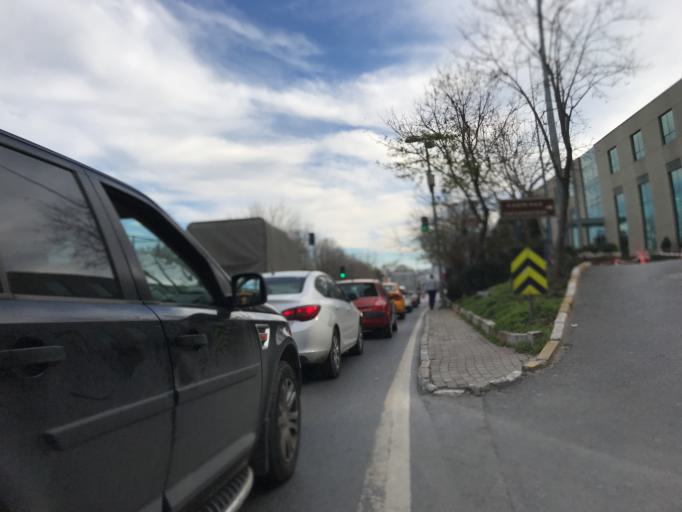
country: TR
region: Istanbul
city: Istanbul
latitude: 41.0248
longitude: 28.9595
